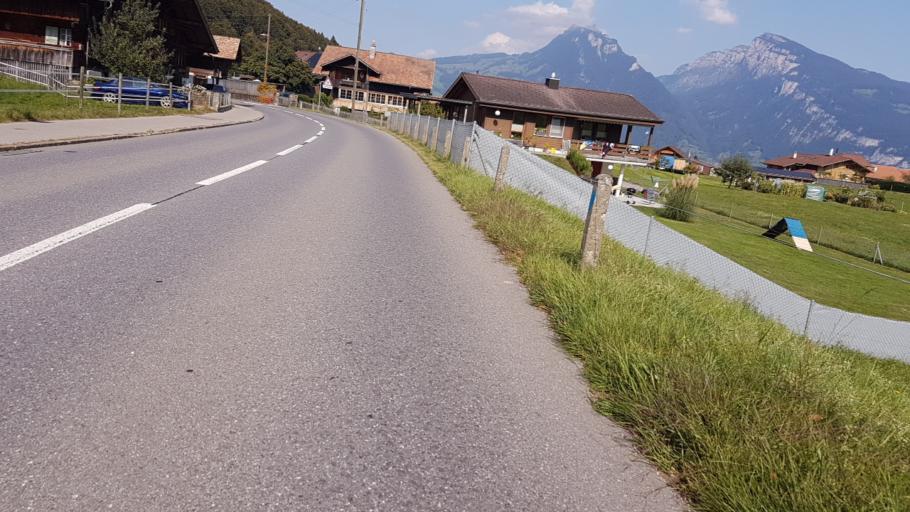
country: CH
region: Bern
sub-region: Frutigen-Niedersimmental District
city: Spiez
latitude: 46.6712
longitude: 7.6803
